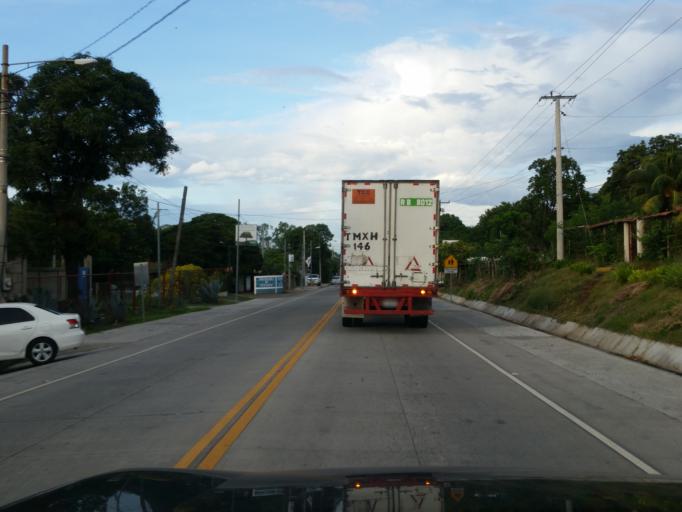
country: NI
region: Managua
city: Ciudad Sandino
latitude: 12.1015
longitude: -86.3396
